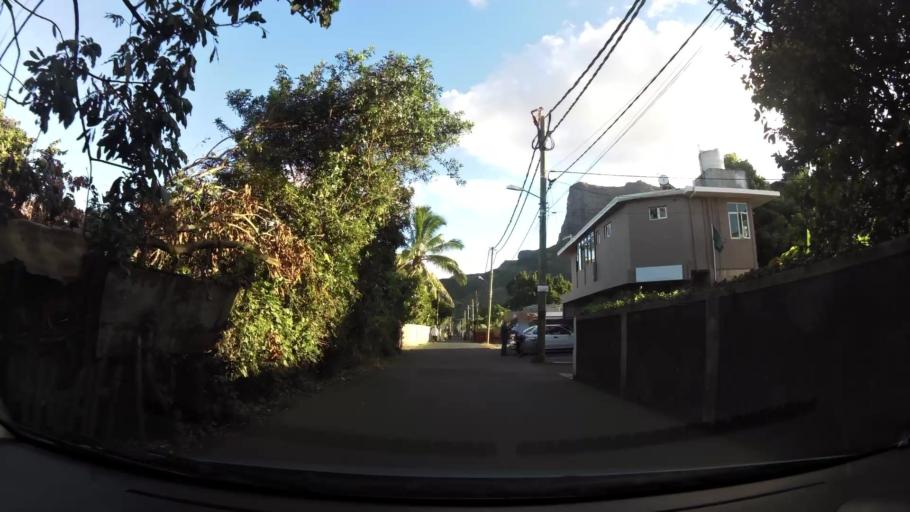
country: MU
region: Plaines Wilhems
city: Quatre Bornes
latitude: -20.2600
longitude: 57.4658
